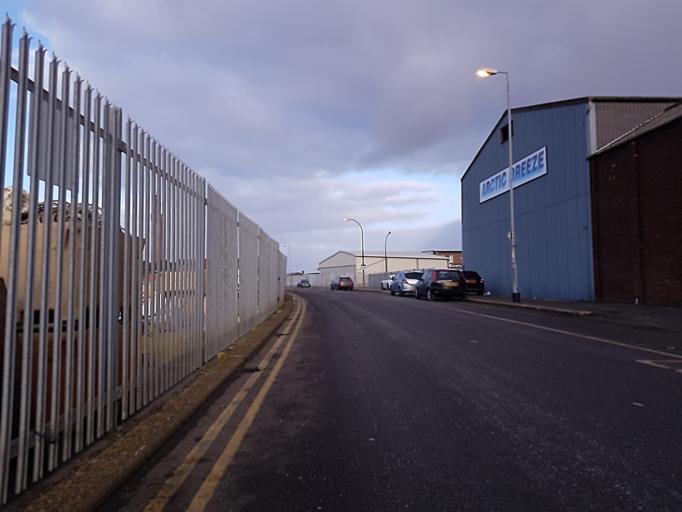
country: GB
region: England
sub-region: North East Lincolnshire
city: Grimsby
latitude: 53.5816
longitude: -0.0626
